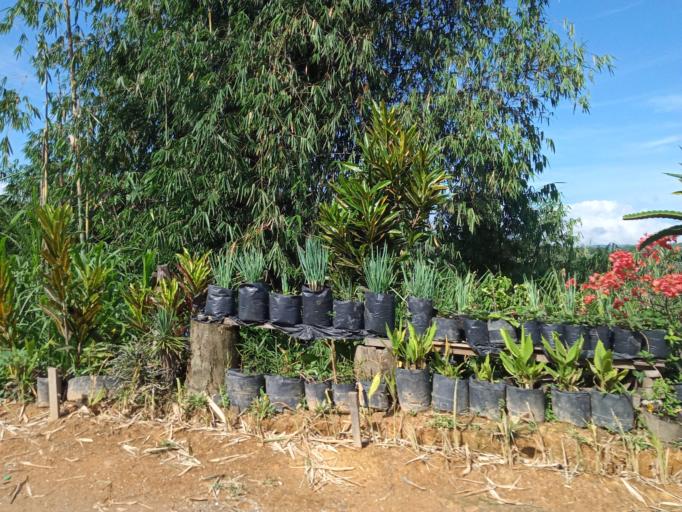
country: ID
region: Jambi
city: Sungai Penuh
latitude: -2.1663
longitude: 101.5960
